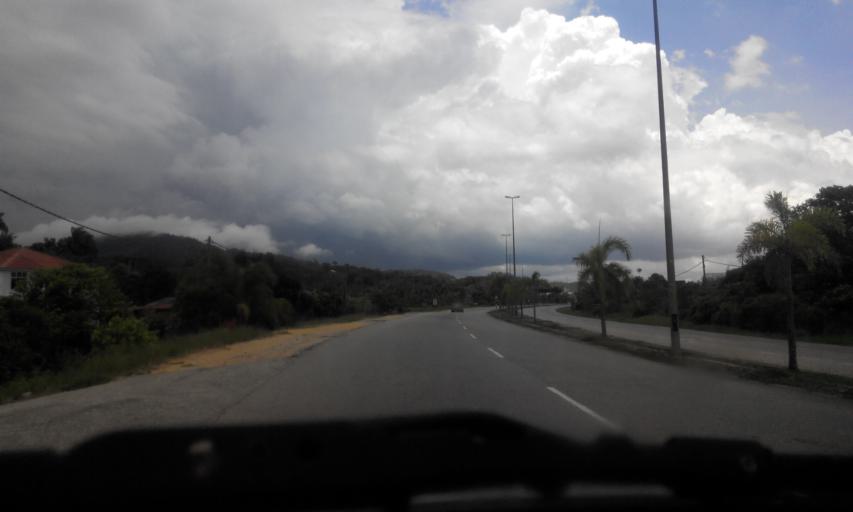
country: MY
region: Perak
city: Parit Buntar
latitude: 5.1281
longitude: 100.5094
